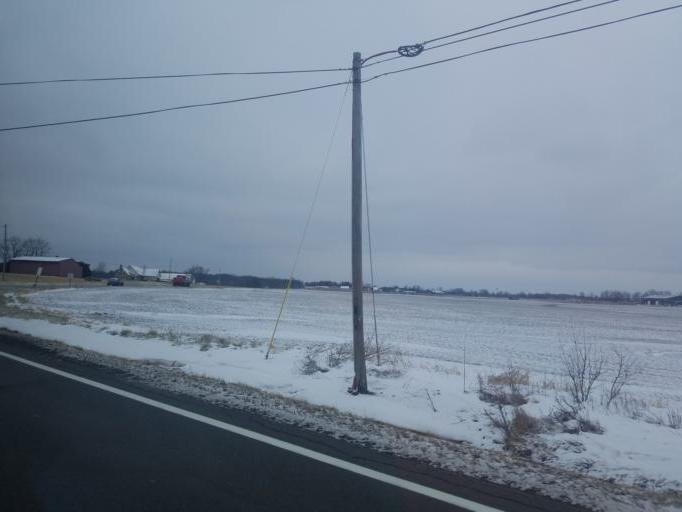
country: US
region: Ohio
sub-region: Licking County
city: Johnstown
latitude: 40.1890
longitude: -82.7568
